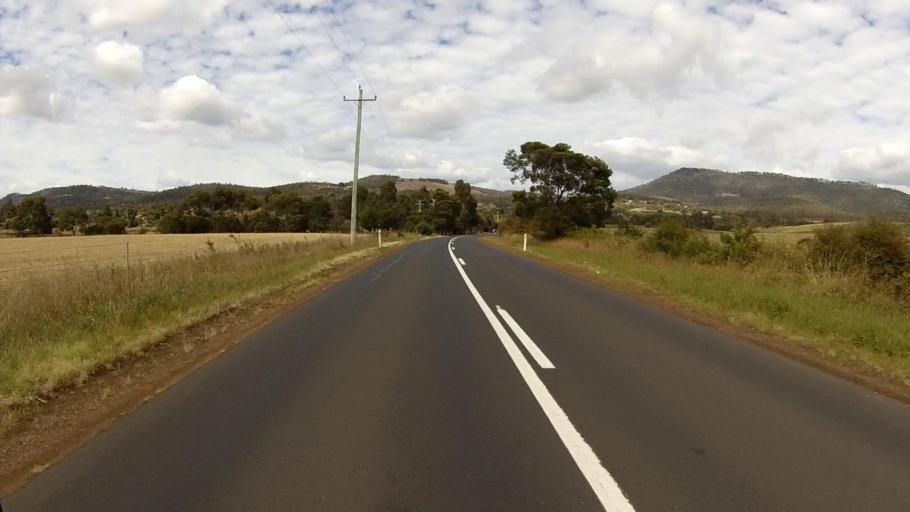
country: AU
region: Tasmania
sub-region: Clarence
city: Cambridge
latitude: -42.7576
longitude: 147.4041
